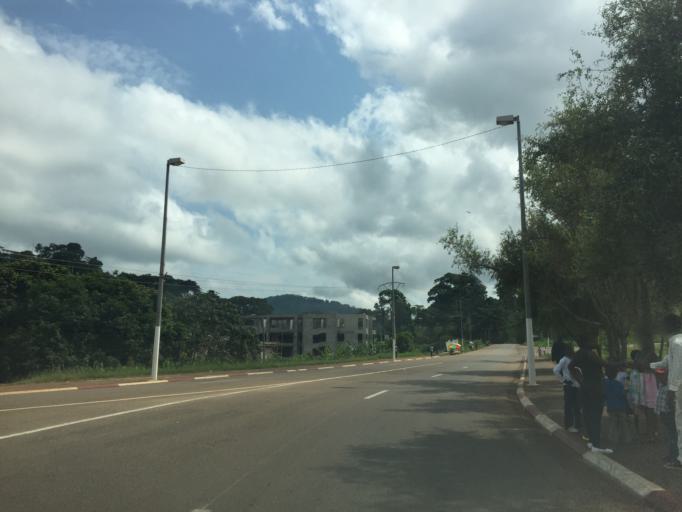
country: CM
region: Centre
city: Yaounde
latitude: 3.9111
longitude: 11.5020
